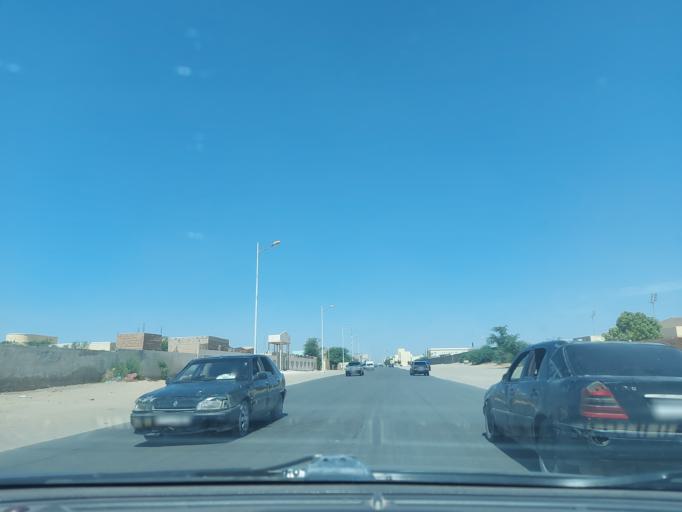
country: MR
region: Nouakchott
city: Nouakchott
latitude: 18.0802
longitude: -15.9694
